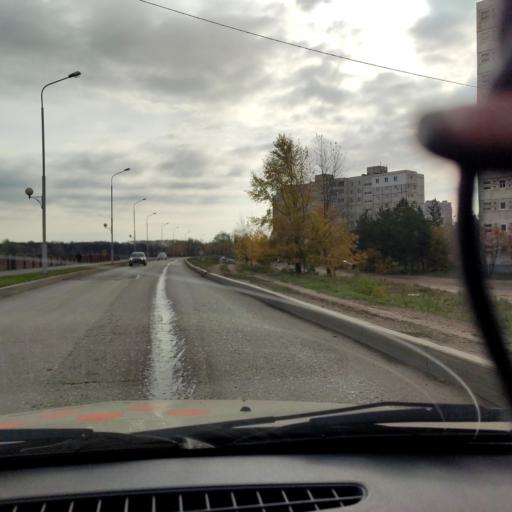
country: RU
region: Bashkortostan
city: Ufa
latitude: 54.7771
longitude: 56.0815
